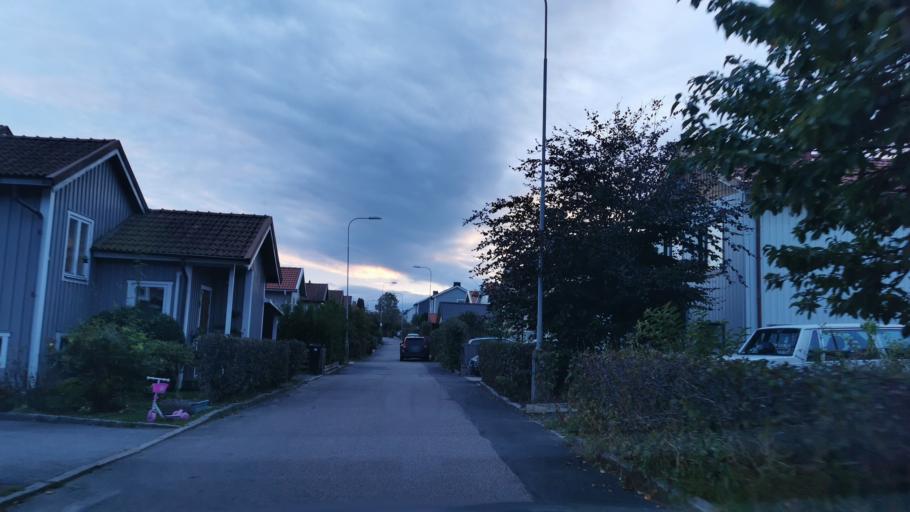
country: SE
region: Vaestra Goetaland
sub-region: Goteborg
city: Eriksbo
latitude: 57.7350
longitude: 12.0597
